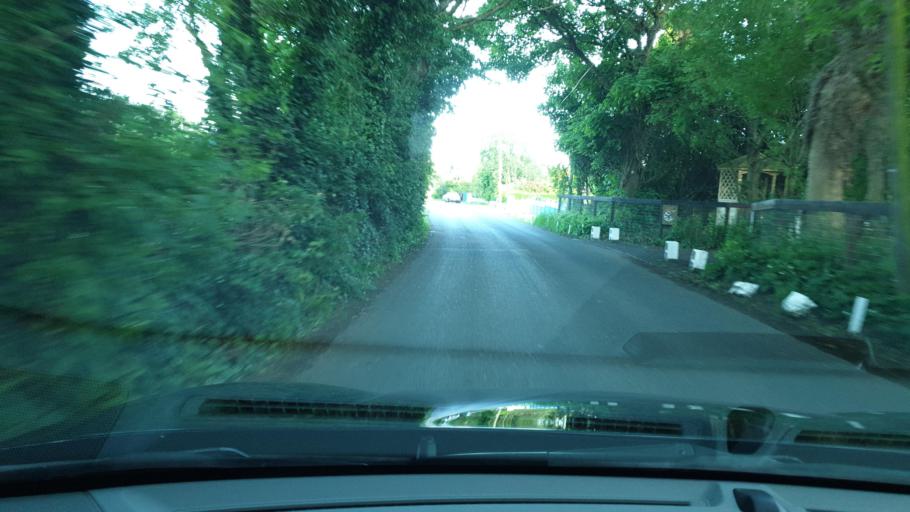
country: IE
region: Leinster
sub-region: An Mhi
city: Ashbourne
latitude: 53.5343
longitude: -6.3160
